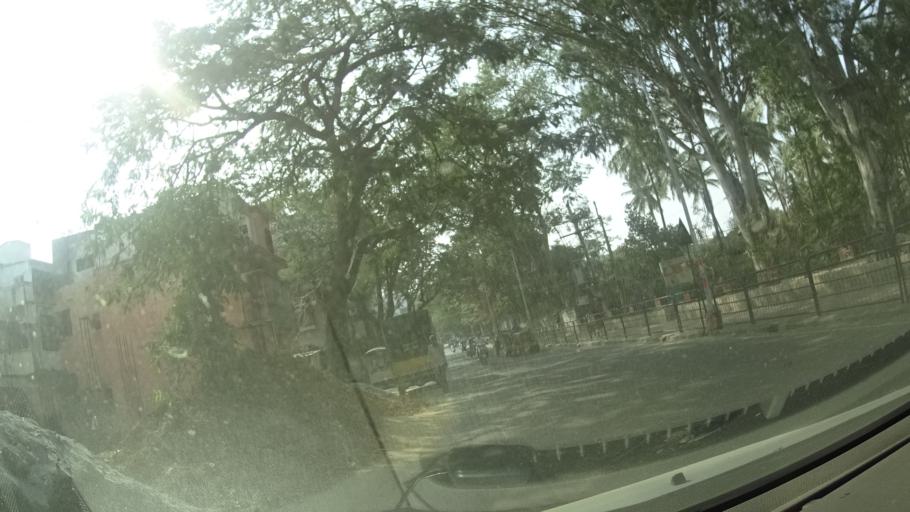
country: IN
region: Karnataka
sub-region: Bangalore Urban
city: Bangalore
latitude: 12.9472
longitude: 77.5662
